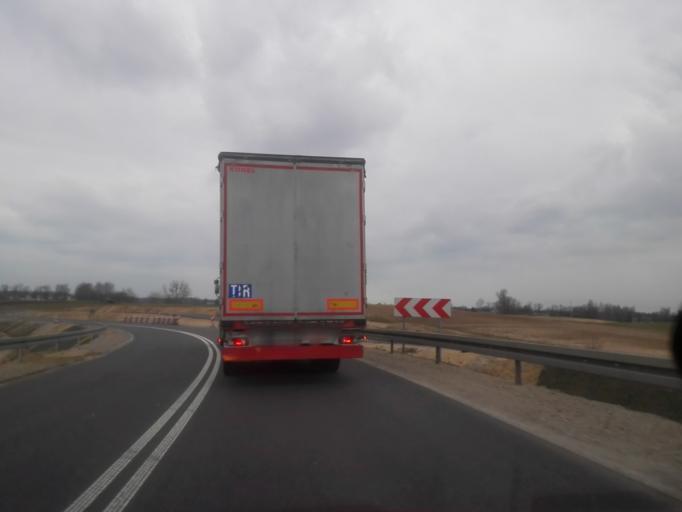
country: PL
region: Podlasie
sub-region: Powiat grajewski
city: Rajgrod
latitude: 53.7786
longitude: 22.8367
